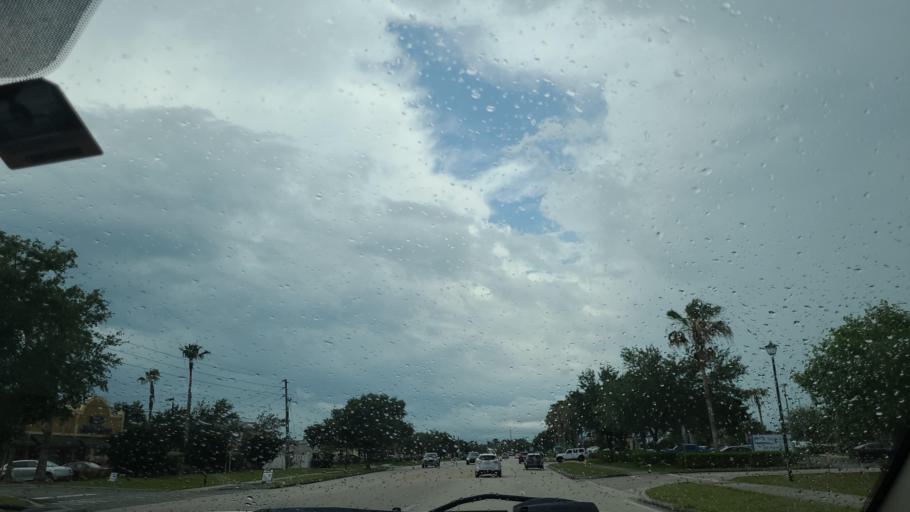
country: US
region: Florida
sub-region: Brevard County
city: Grant-Valkaria
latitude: 27.9513
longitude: -80.6557
